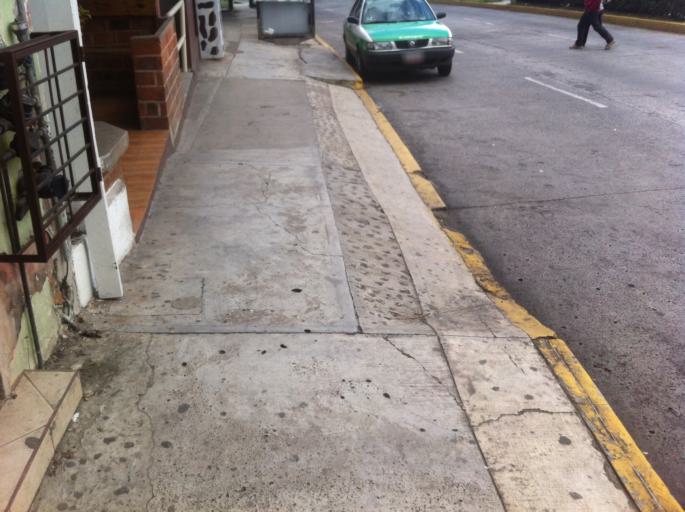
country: MX
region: Veracruz
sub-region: Xalapa
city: Xalapa de Enriquez
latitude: 19.5255
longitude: -96.8995
